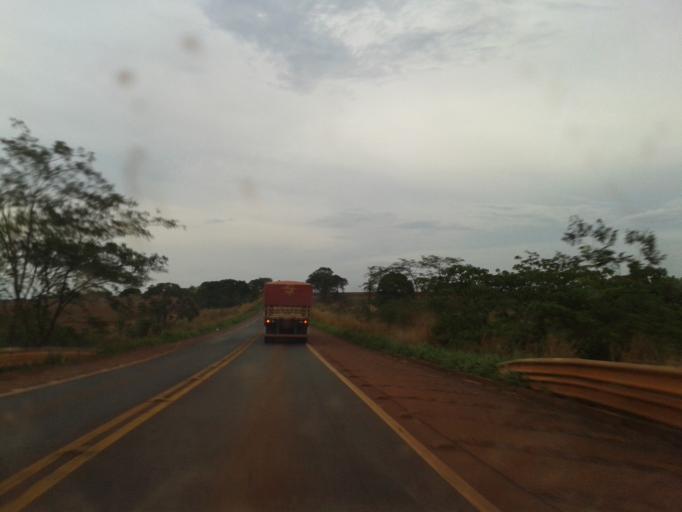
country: BR
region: Goias
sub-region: Santa Helena De Goias
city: Santa Helena de Goias
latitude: -17.9520
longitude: -50.5102
